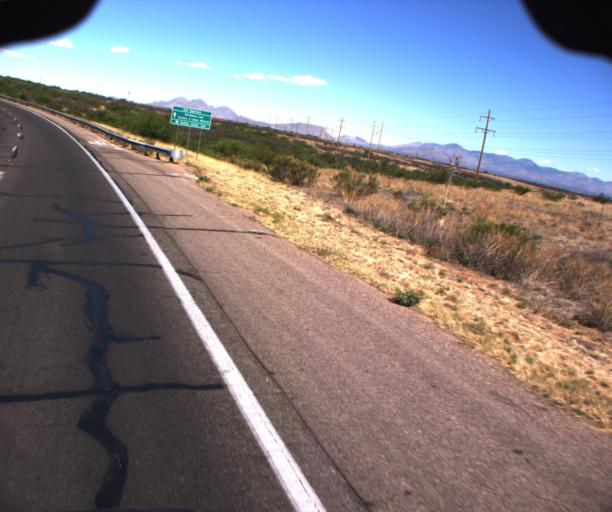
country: US
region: Arizona
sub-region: Cochise County
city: Sierra Vista
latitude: 31.5738
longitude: -110.3117
